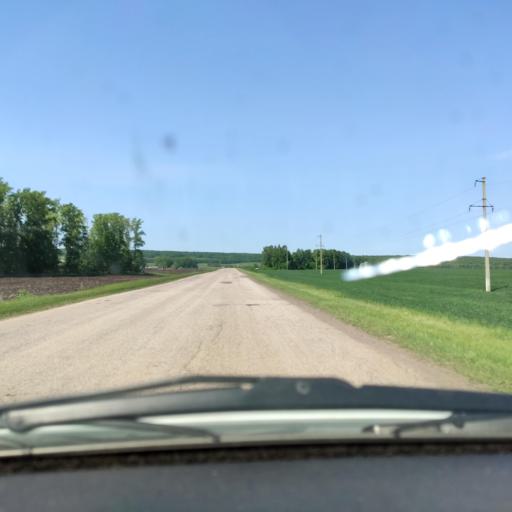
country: RU
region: Bashkortostan
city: Chishmy
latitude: 54.4676
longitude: 55.5412
